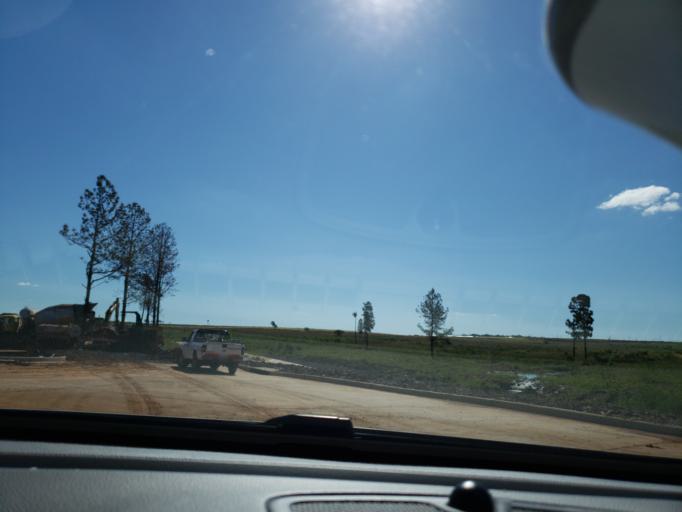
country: AR
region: Misiones
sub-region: Departamento de Capital
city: Posadas
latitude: -27.3977
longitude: -55.9901
